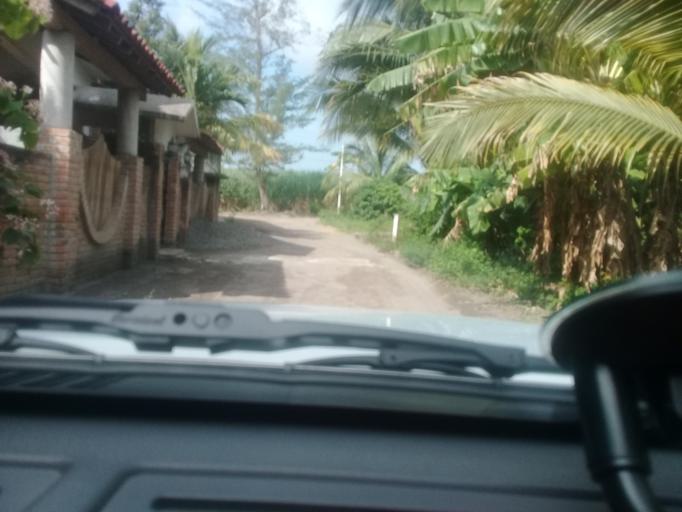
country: MX
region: Veracruz
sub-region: Paso de Ovejas
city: Tolome
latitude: 19.2688
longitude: -96.3860
